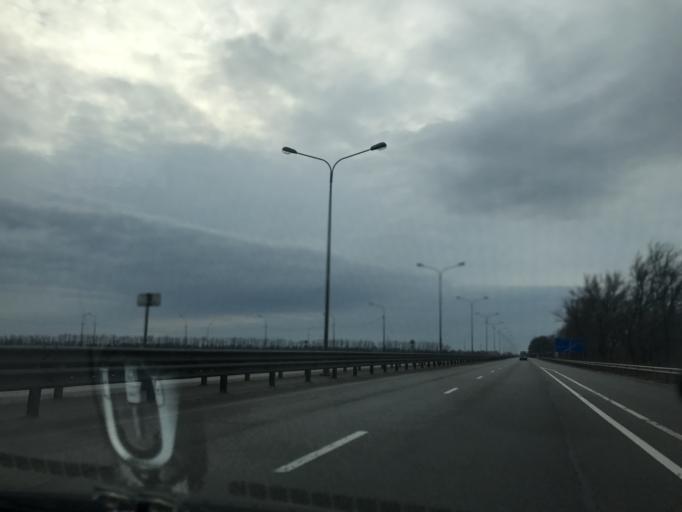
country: RU
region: Krasnodarskiy
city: Tikhoretsk
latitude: 45.8879
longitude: 40.1290
